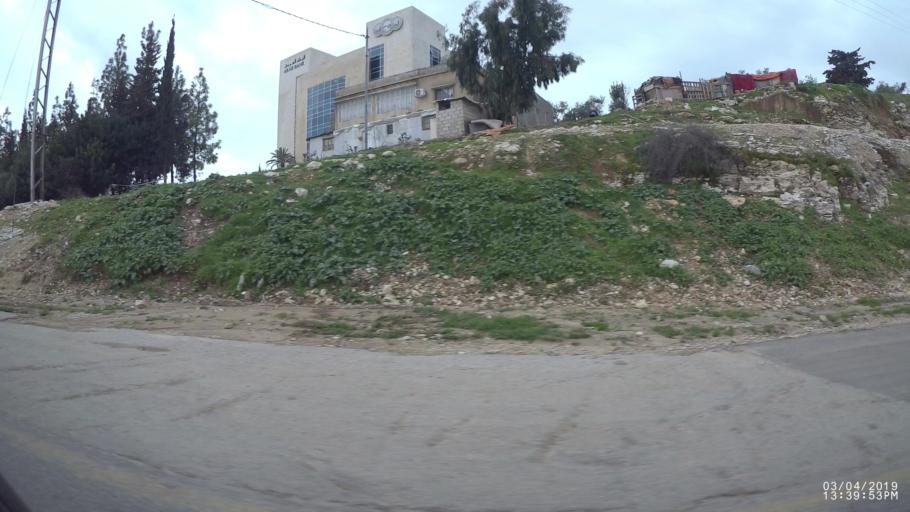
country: JO
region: Amman
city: Wadi as Sir
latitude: 31.9338
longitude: 35.8550
